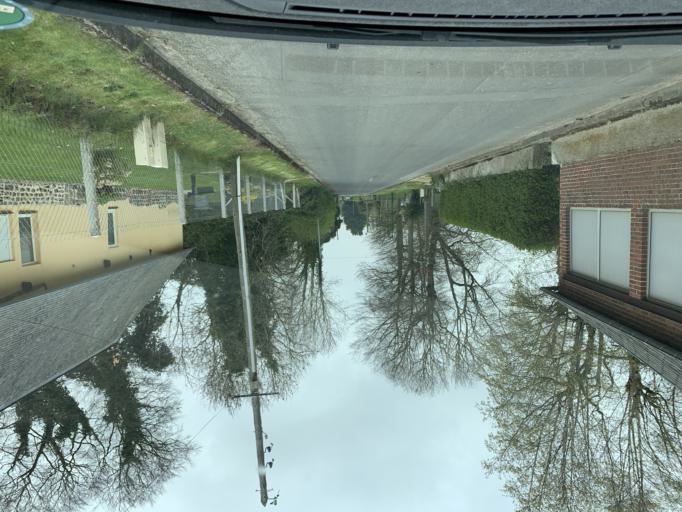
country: FR
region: Haute-Normandie
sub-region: Departement de la Seine-Maritime
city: Saint-Valery-en-Caux
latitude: 49.8544
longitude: 0.7949
